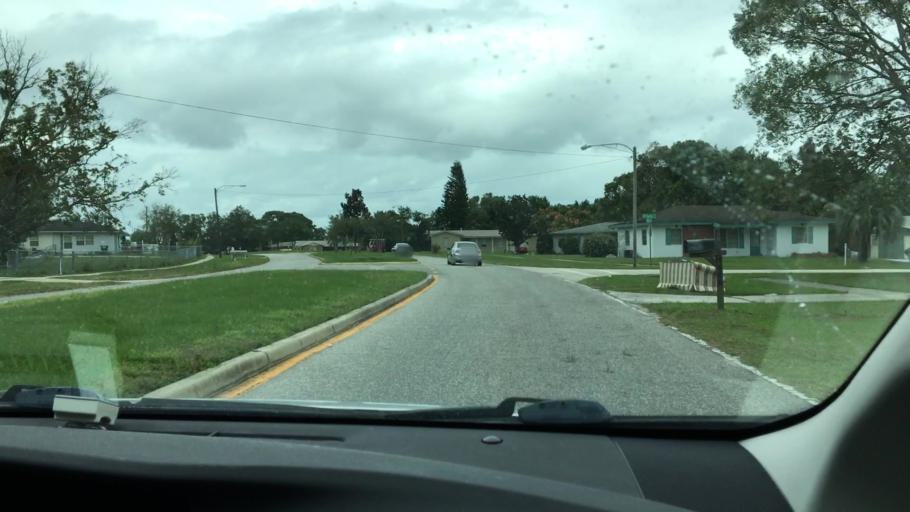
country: US
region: Florida
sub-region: Volusia County
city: Deltona
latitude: 28.8986
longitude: -81.2288
